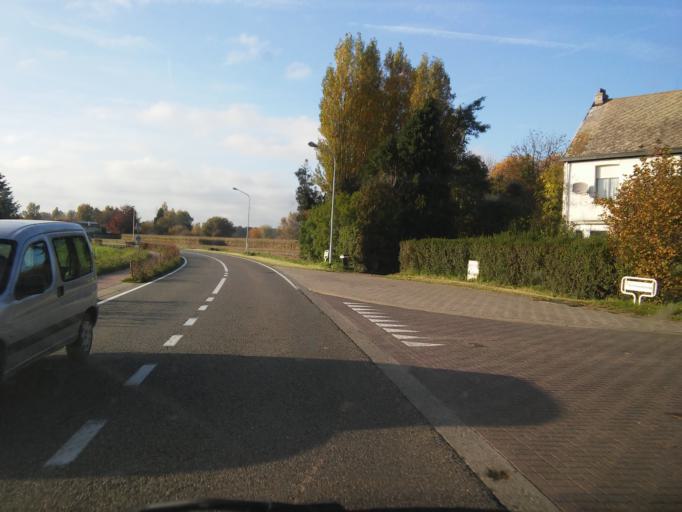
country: BE
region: Flanders
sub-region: Provincie Antwerpen
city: Duffel
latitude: 51.1000
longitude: 4.4828
